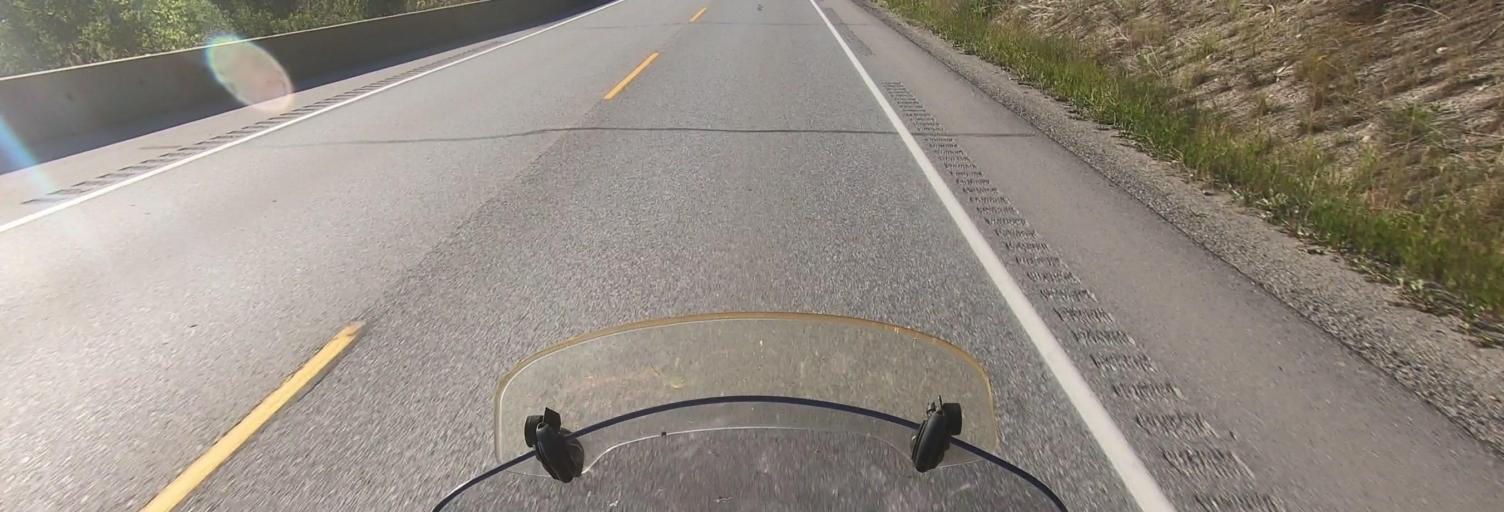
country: CA
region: British Columbia
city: Golden
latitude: 51.4530
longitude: -117.1019
